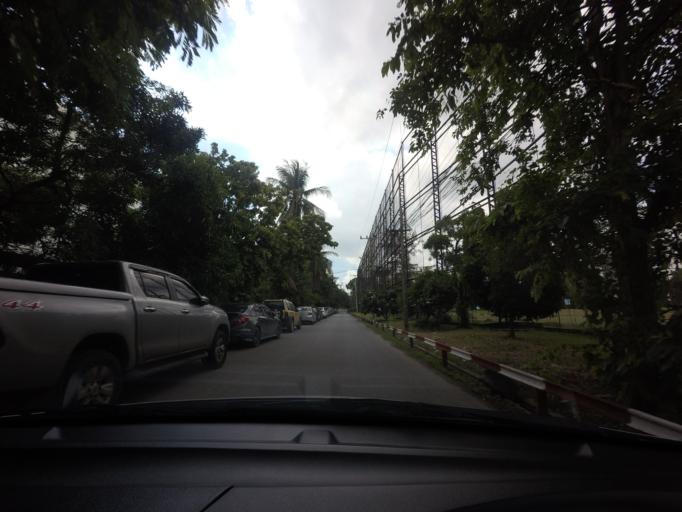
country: TH
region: Bangkok
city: Chatuchak
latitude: 13.8182
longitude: 100.5546
